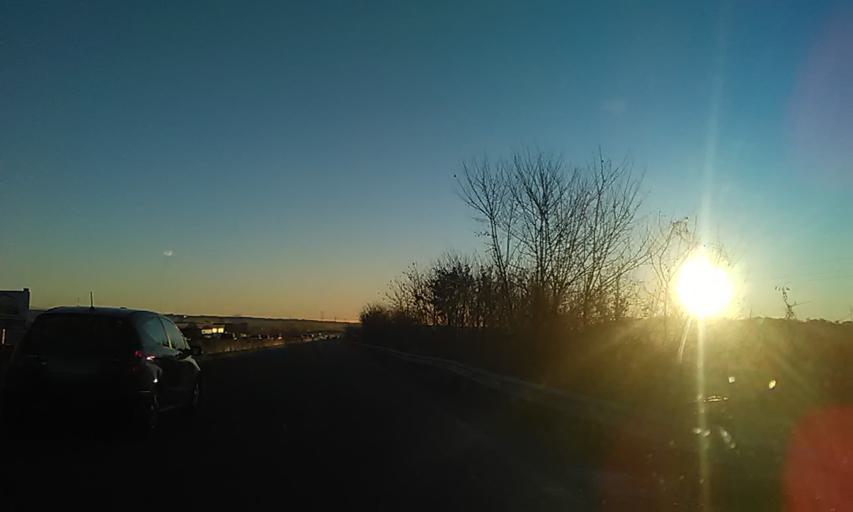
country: IT
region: Piedmont
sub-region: Provincia di Biella
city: Vigliano Biellese
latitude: 45.5554
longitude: 8.1178
